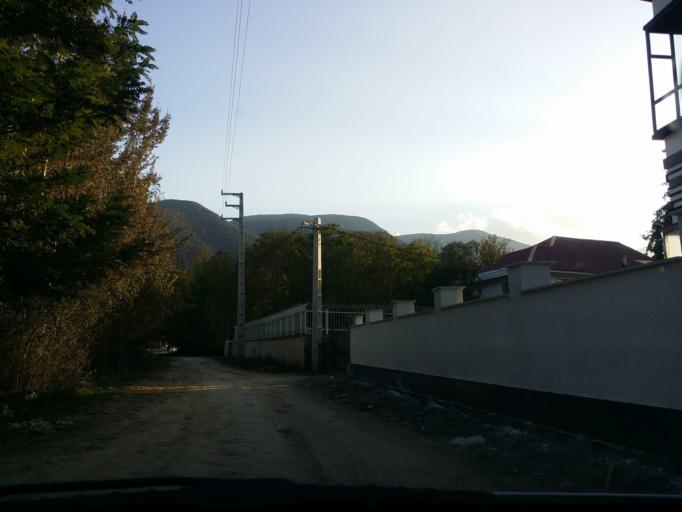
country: IR
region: Mazandaran
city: `Abbasabad
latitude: 36.5136
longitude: 51.1900
